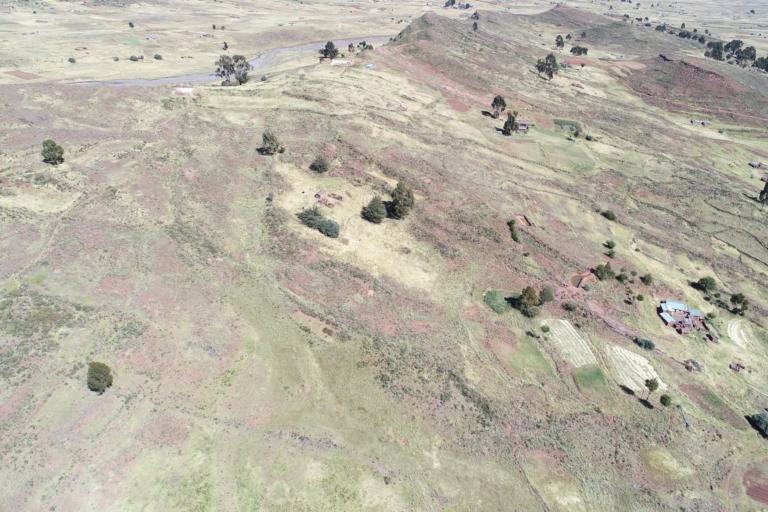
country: BO
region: La Paz
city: Tiahuanaco
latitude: -16.6079
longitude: -68.7620
